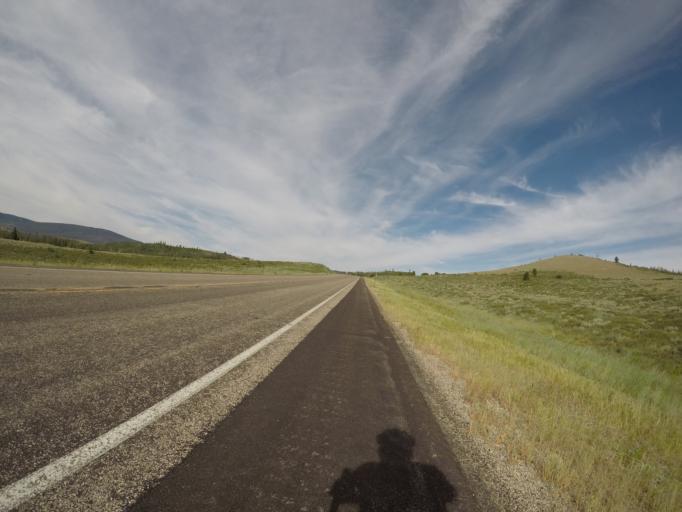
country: US
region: Wyoming
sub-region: Carbon County
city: Saratoga
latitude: 41.1818
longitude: -106.8706
